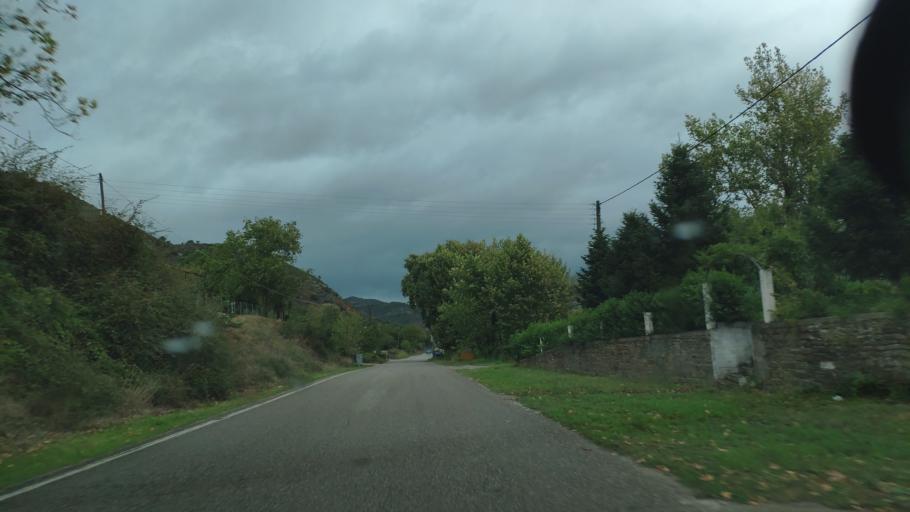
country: GR
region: West Greece
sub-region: Nomos Aitolias kai Akarnanias
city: Krikellos
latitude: 38.9922
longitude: 21.3145
